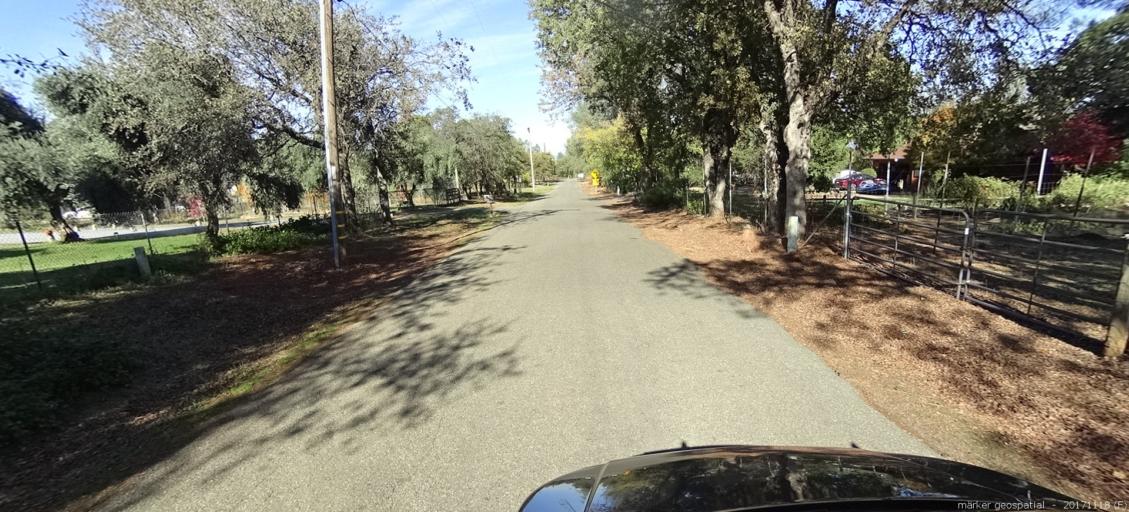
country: US
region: California
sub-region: Shasta County
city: Anderson
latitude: 40.4546
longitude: -122.4356
